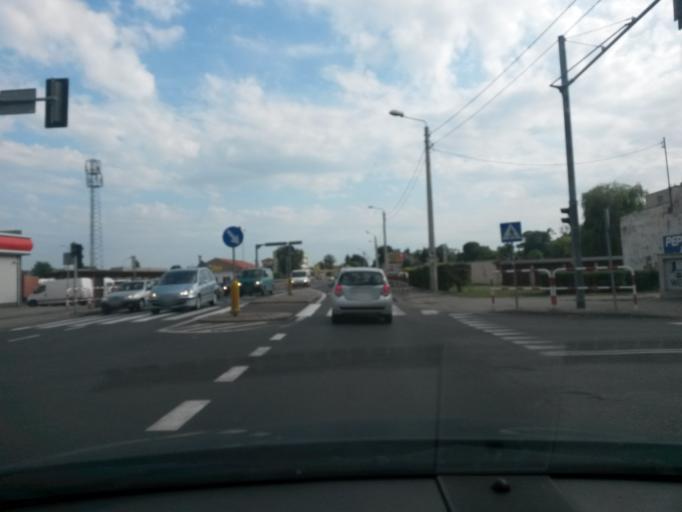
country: PL
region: Greater Poland Voivodeship
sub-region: Powiat rawicki
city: Rawicz
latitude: 51.6151
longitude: 16.8669
